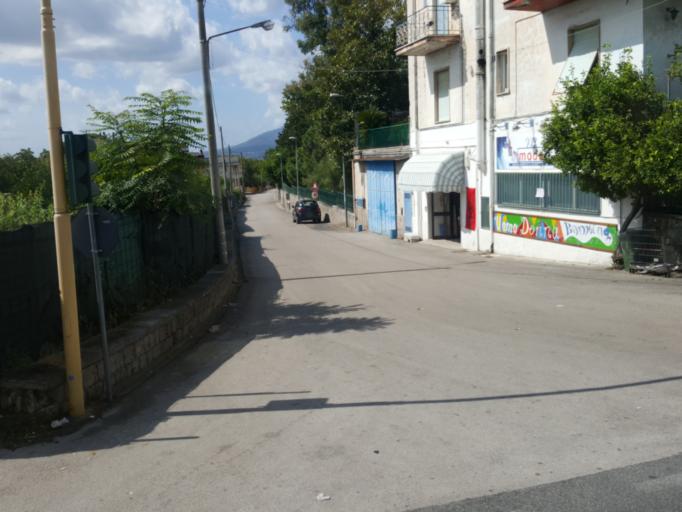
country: IT
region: Campania
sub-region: Provincia di Napoli
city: Liveri
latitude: 40.9040
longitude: 14.5636
